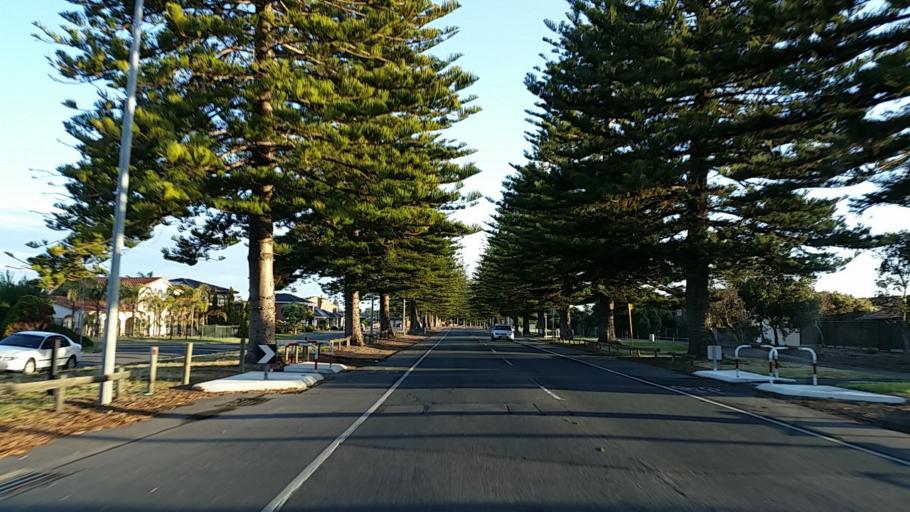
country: AU
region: South Australia
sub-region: Port Adelaide Enfield
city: Birkenhead
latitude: -34.7896
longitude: 138.4904
